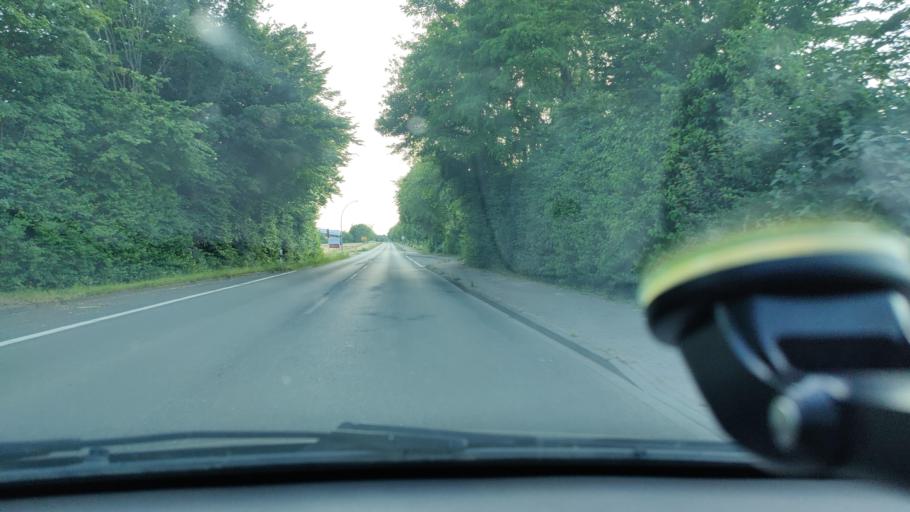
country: DE
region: North Rhine-Westphalia
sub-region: Regierungsbezirk Munster
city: Coesfeld
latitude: 52.0169
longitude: 7.1986
